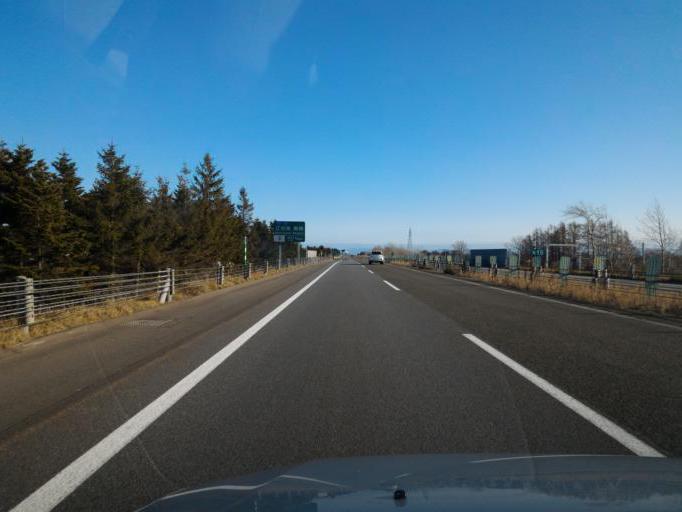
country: JP
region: Hokkaido
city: Ebetsu
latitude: 43.0983
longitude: 141.5871
